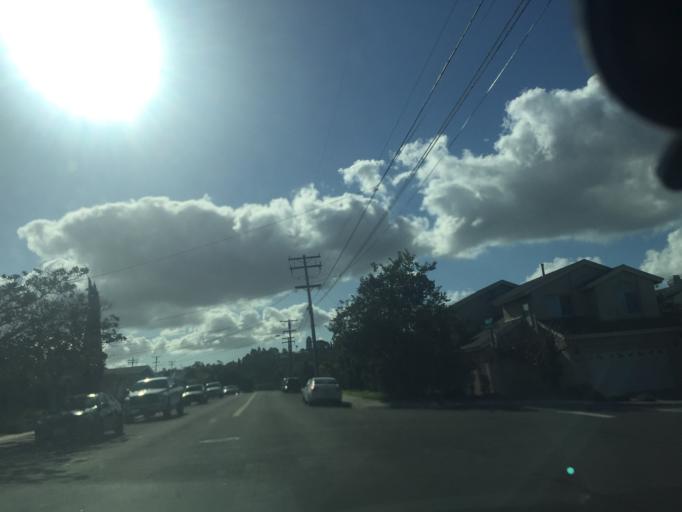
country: US
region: California
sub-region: San Diego County
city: La Mesa
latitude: 32.7867
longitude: -117.0939
